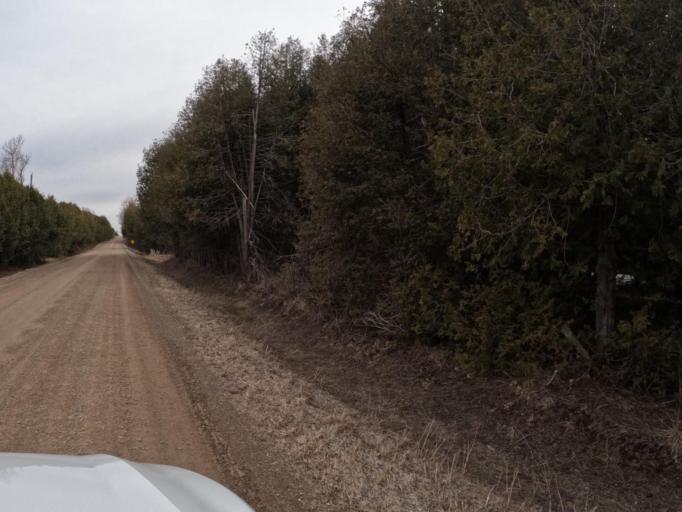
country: CA
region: Ontario
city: Shelburne
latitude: 43.9415
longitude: -80.2602
